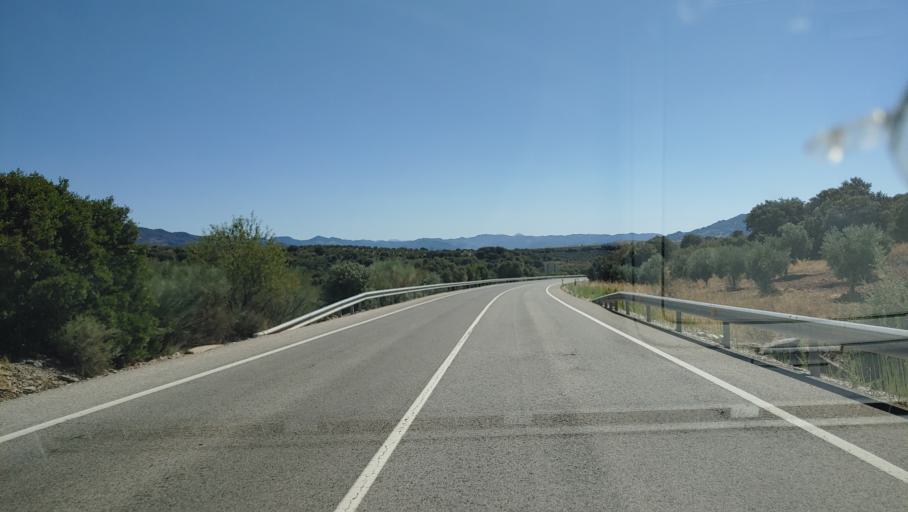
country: ES
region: Andalusia
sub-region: Provincia de Jaen
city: Genave
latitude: 38.4654
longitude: -2.7616
